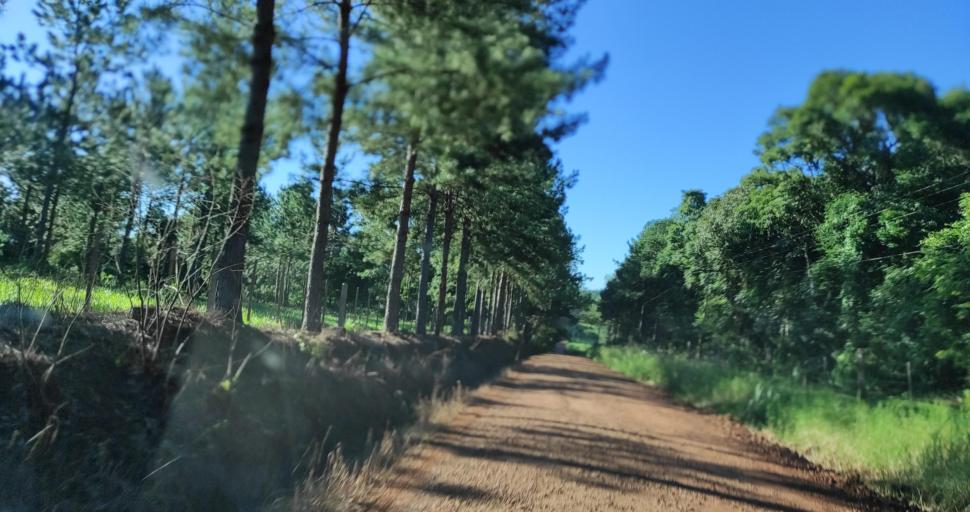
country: AR
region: Misiones
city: Puerto Rico
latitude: -26.8400
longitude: -55.0024
